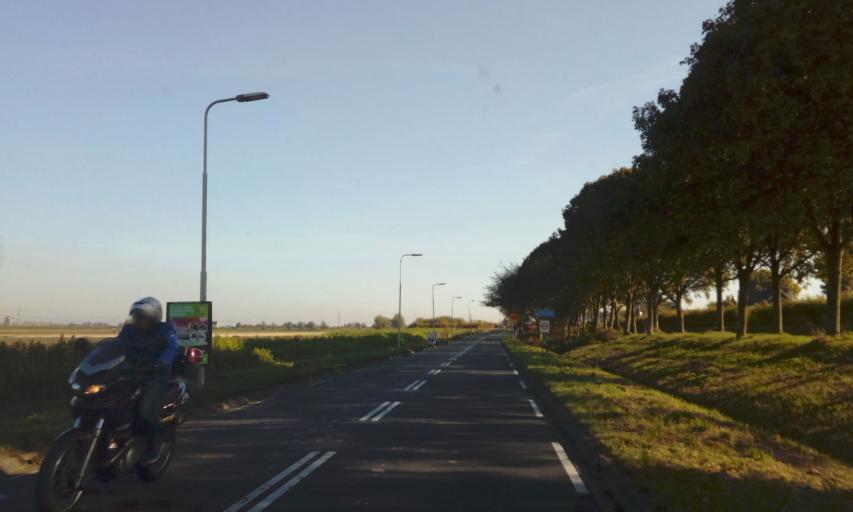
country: NL
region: South Holland
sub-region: Gemeente Lansingerland
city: Bleiswijk
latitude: 52.0174
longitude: 4.5428
